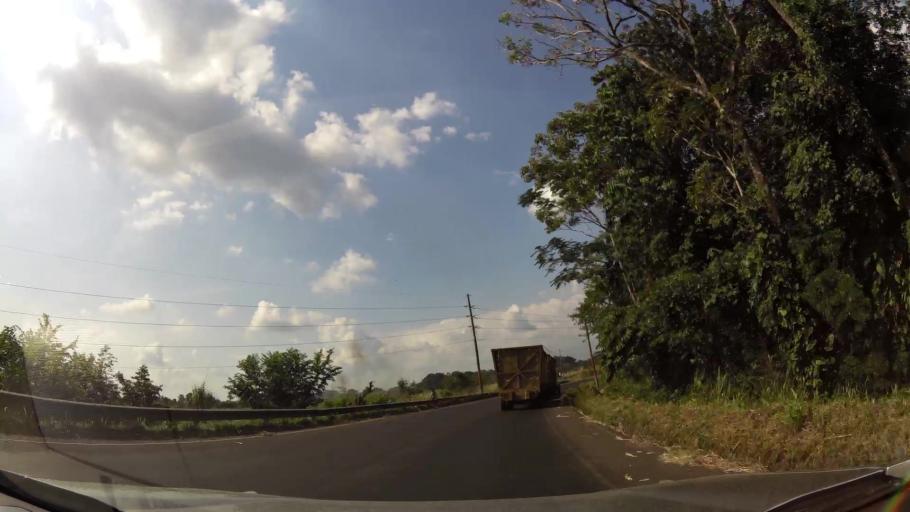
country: GT
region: Retalhuleu
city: San Sebastian
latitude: 14.5528
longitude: -91.6395
